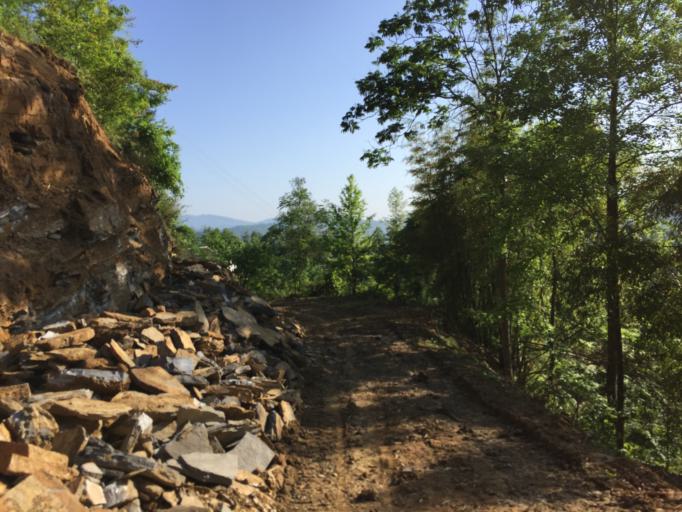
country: CN
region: Guizhou Sheng
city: Xujiaba
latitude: 27.7107
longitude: 108.0189
